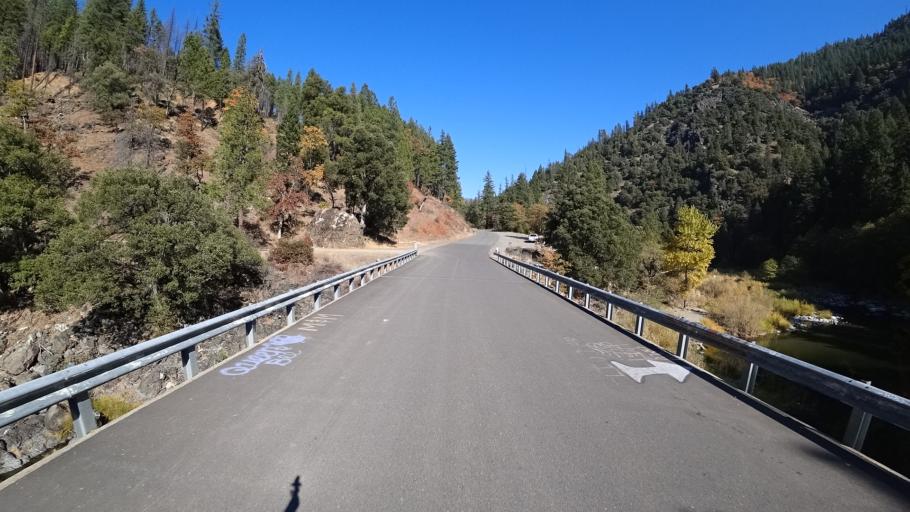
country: US
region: California
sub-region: Siskiyou County
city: Happy Camp
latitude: 41.6485
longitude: -123.1138
